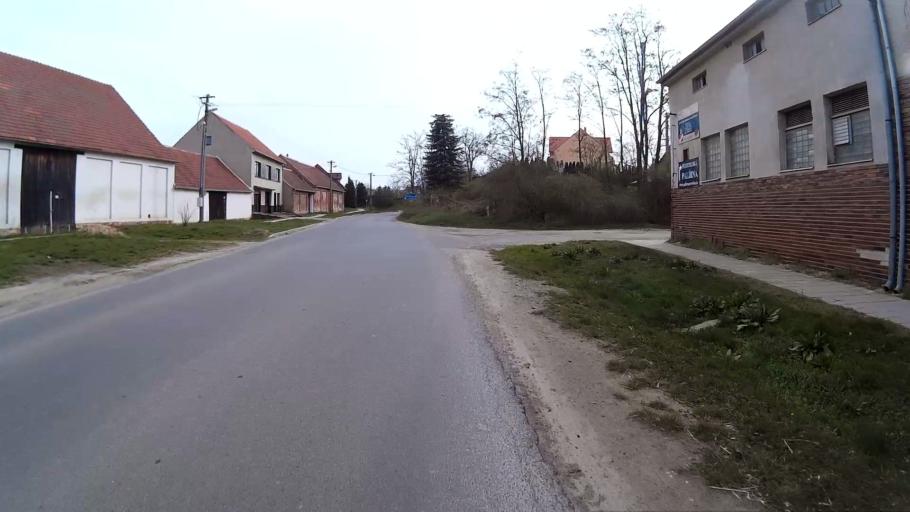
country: CZ
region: South Moravian
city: Orechov
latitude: 49.0792
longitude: 16.5452
